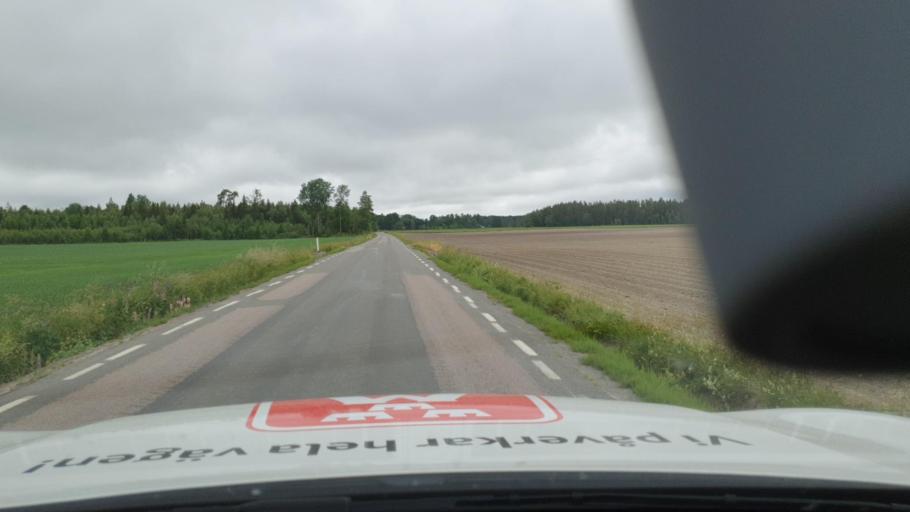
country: SE
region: Vaestra Goetaland
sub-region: Tibro Kommun
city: Tibro
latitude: 58.3985
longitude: 14.0654
